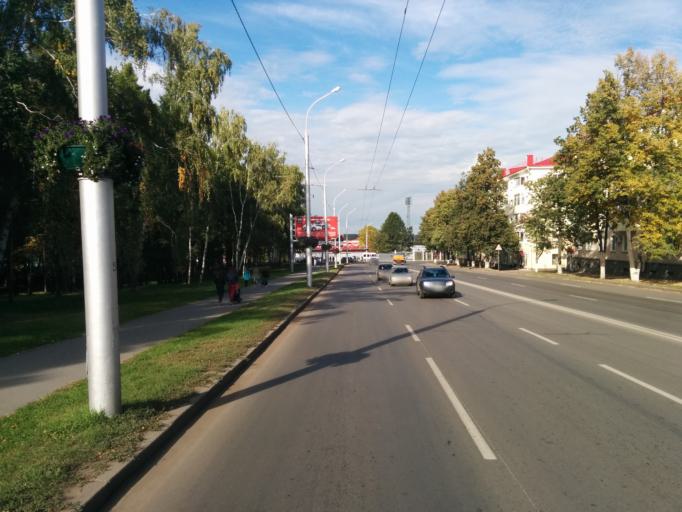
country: RU
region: Bashkortostan
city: Ufa
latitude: 54.8230
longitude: 56.0594
